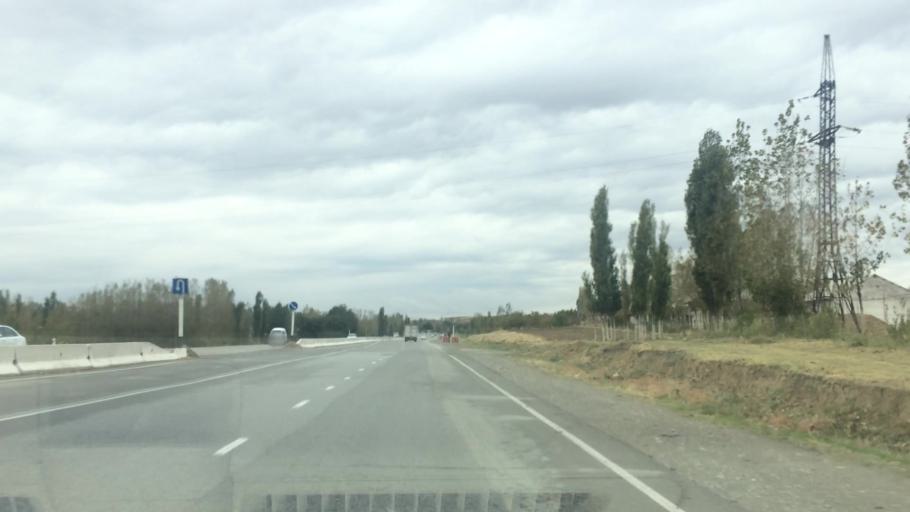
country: UZ
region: Jizzax
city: Jizzax
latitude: 39.9612
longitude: 67.5469
